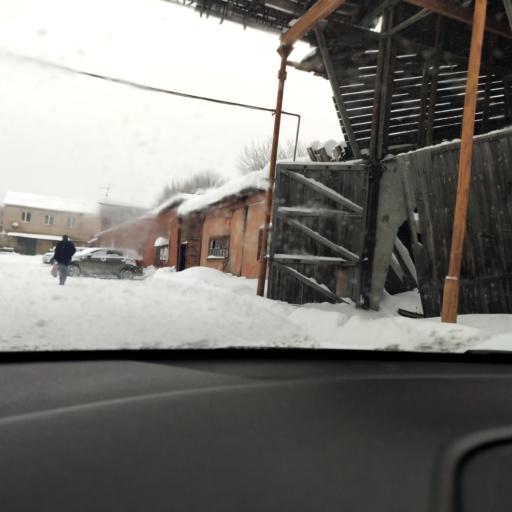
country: RU
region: Tatarstan
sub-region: Gorod Kazan'
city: Kazan
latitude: 55.7790
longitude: 49.1773
